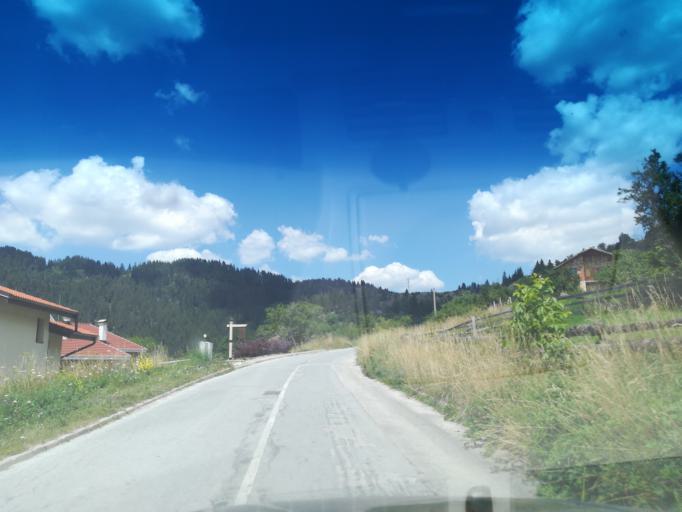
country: BG
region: Smolyan
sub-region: Obshtina Smolyan
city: Smolyan
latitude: 41.6632
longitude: 24.7740
